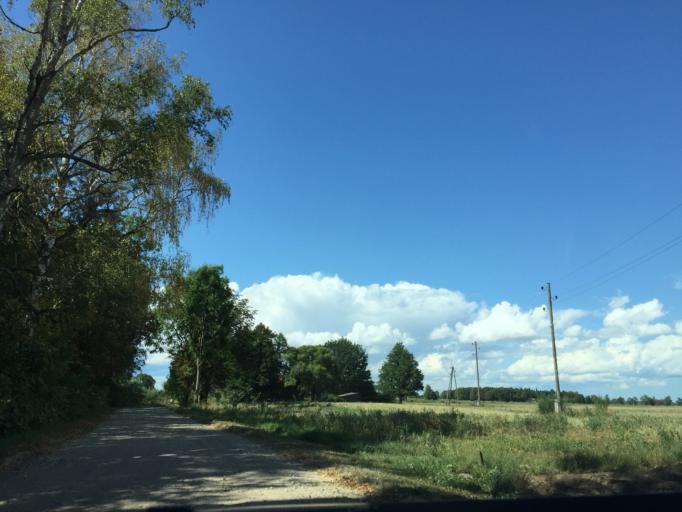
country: LT
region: Siauliu apskritis
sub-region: Joniskis
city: Joniskis
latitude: 56.3412
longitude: 23.5544
